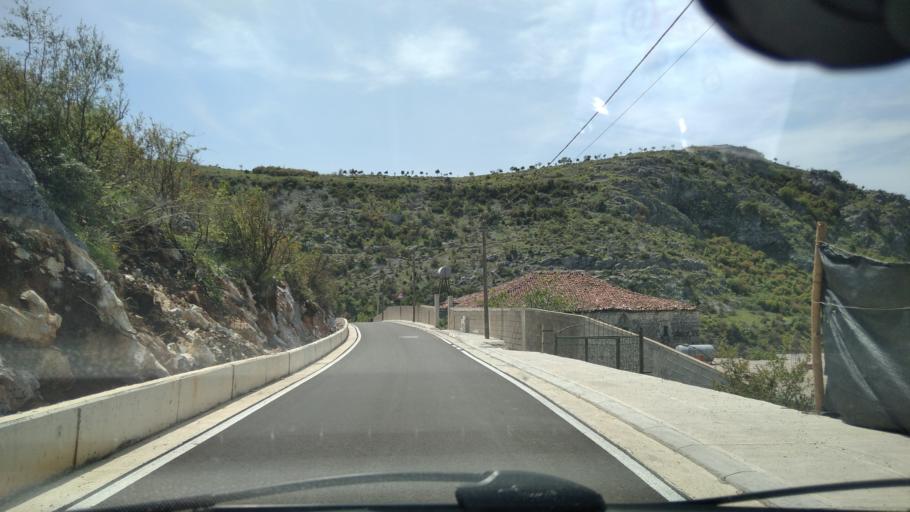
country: AL
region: Shkoder
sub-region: Rrethi i Shkodres
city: Guri i Zi
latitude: 42.1238
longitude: 19.6063
